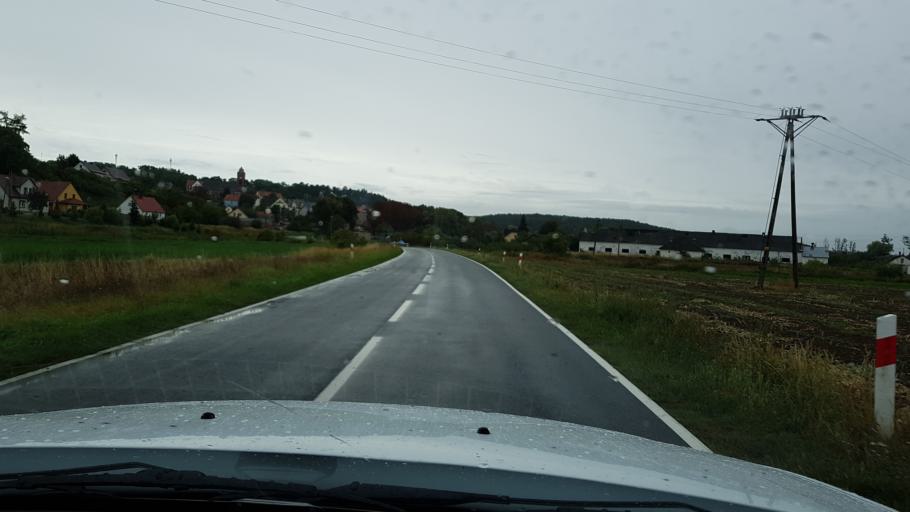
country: PL
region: West Pomeranian Voivodeship
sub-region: Powiat gryfinski
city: Cedynia
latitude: 52.8827
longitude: 14.2019
